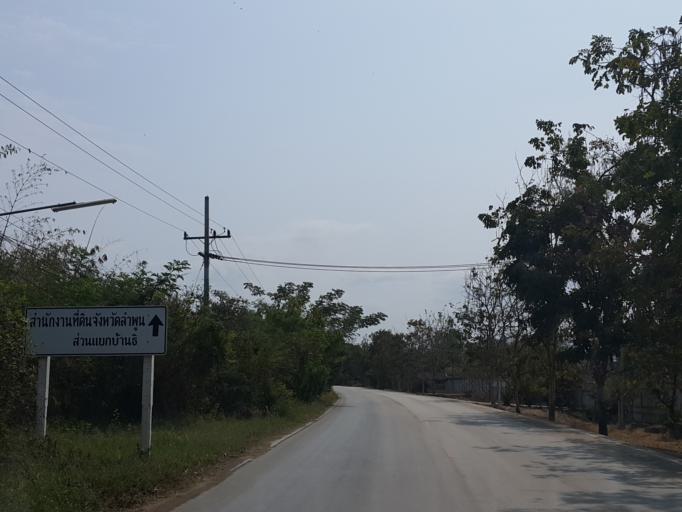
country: TH
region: Lamphun
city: Ban Thi
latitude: 18.6650
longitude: 99.0983
